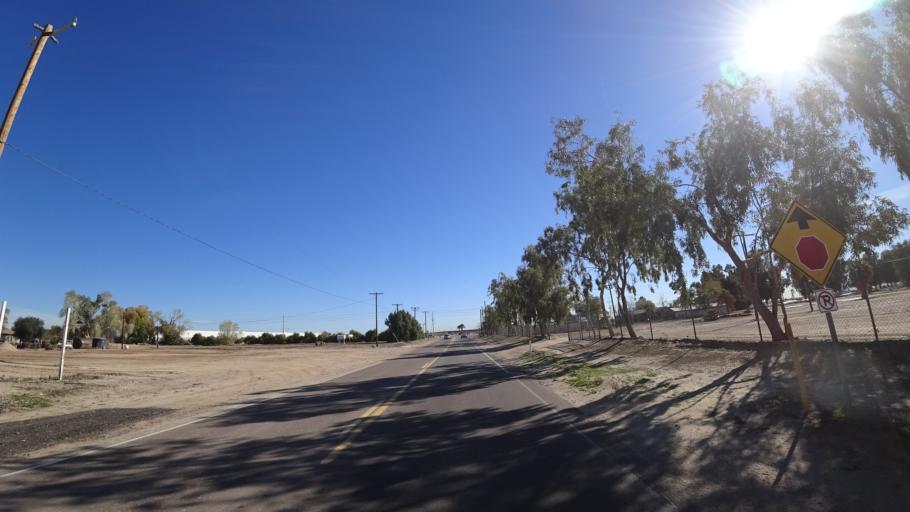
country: US
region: Arizona
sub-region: Maricopa County
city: Citrus Park
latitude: 33.4937
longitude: -112.4291
